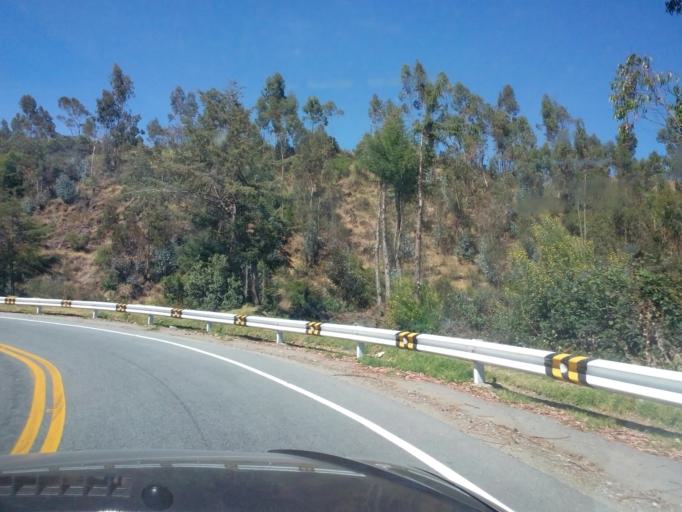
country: PE
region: Cusco
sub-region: Provincia de Anta
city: Limatambo
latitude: -13.4510
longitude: -72.3972
